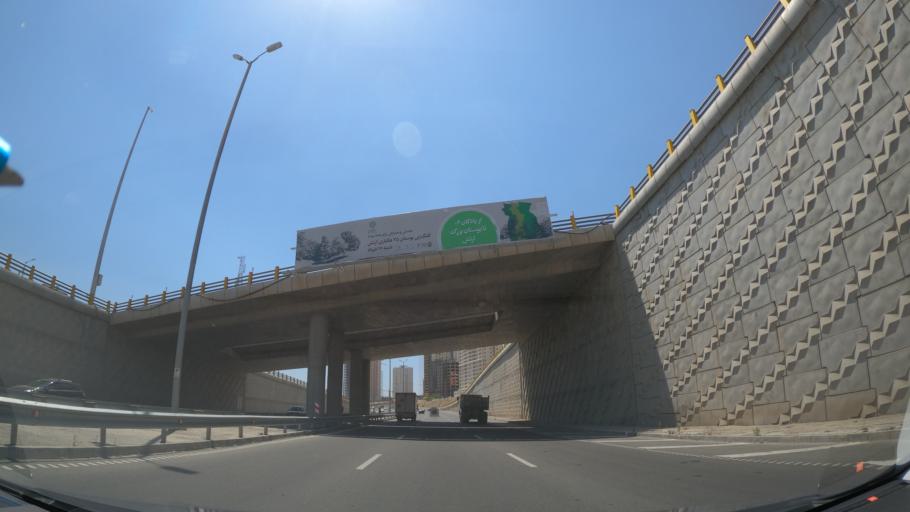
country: IR
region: Tehran
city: Shahr-e Qods
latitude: 35.7523
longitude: 51.1440
